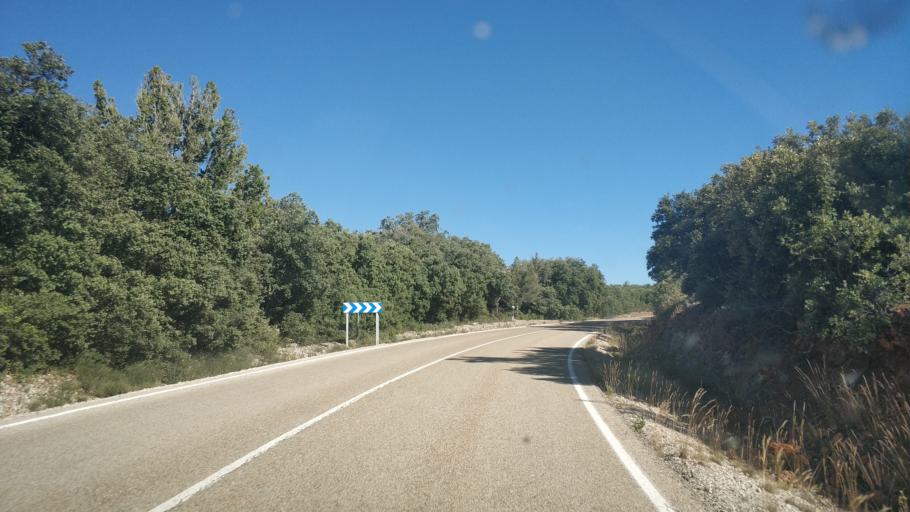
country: ES
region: Castille and Leon
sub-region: Provincia de Soria
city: Montejo de Tiermes
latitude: 41.4137
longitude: -3.2018
